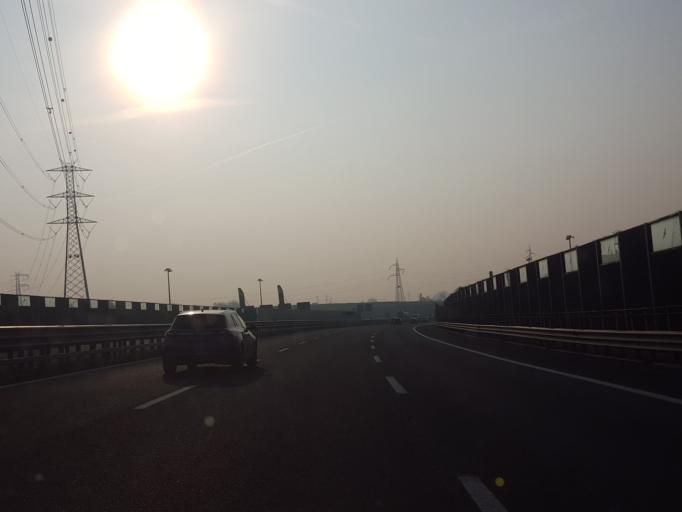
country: IT
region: Veneto
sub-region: Provincia di Venezia
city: Marano
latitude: 45.4791
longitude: 12.1296
